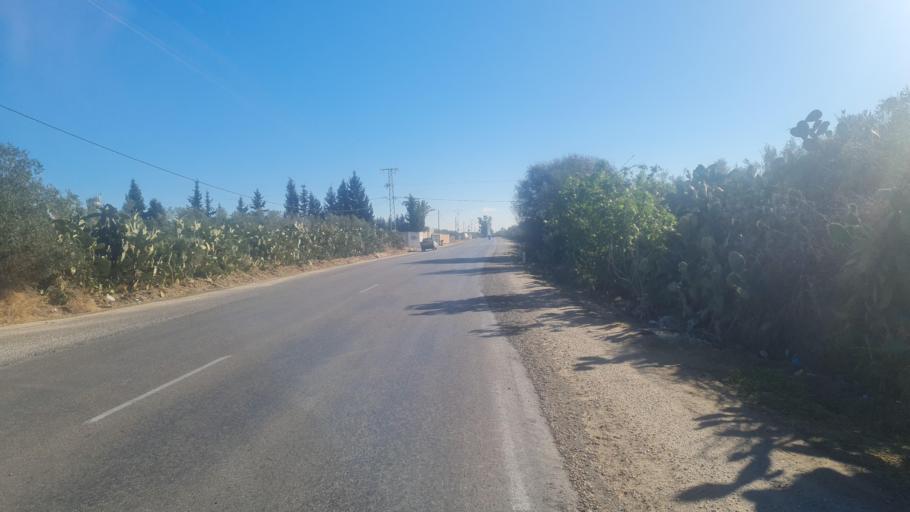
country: TN
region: Susah
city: Sidi Bou Ali
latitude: 35.9093
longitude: 10.3804
